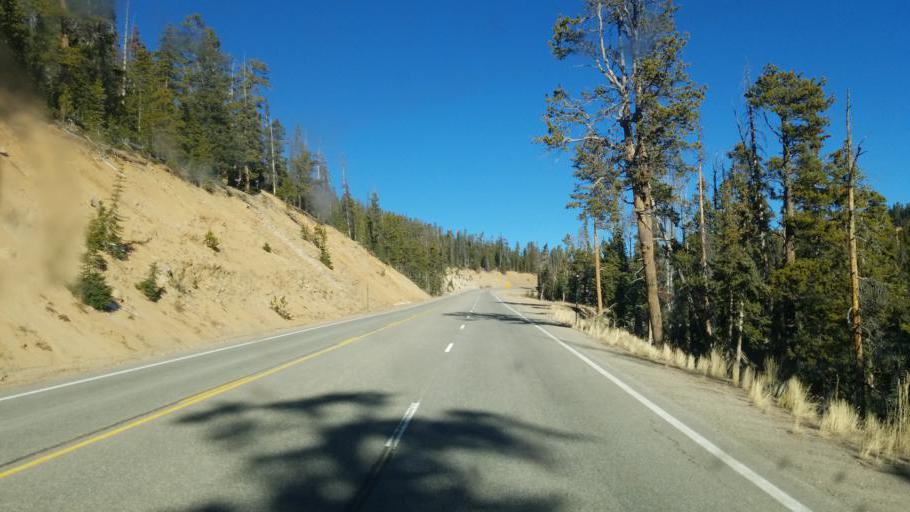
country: US
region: Colorado
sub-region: Chaffee County
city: Salida
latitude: 38.4813
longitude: -106.3378
